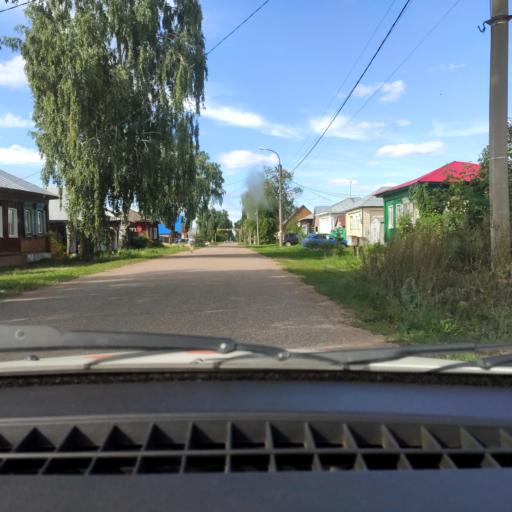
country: RU
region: Bashkortostan
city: Blagoveshchensk
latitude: 55.0277
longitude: 55.9804
